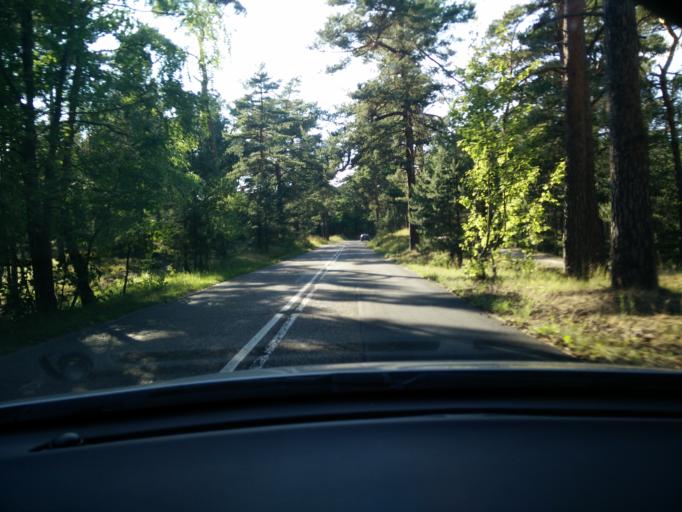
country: PL
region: Pomeranian Voivodeship
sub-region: Powiat pucki
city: Hel
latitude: 54.6500
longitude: 18.7618
